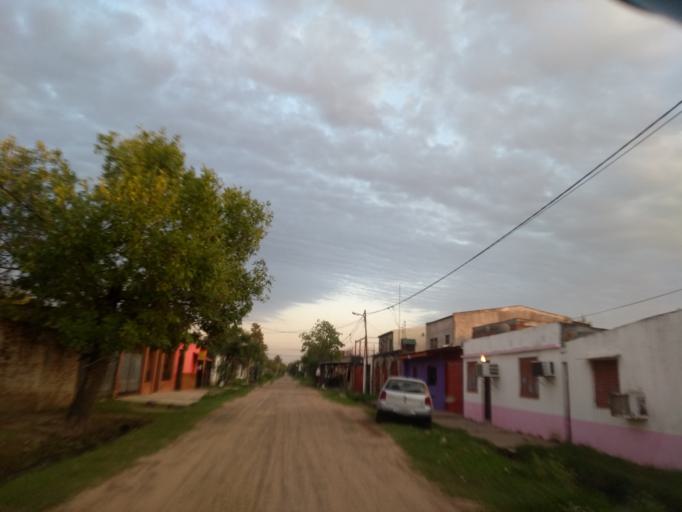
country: AR
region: Chaco
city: Resistencia
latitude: -27.4770
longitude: -58.9761
